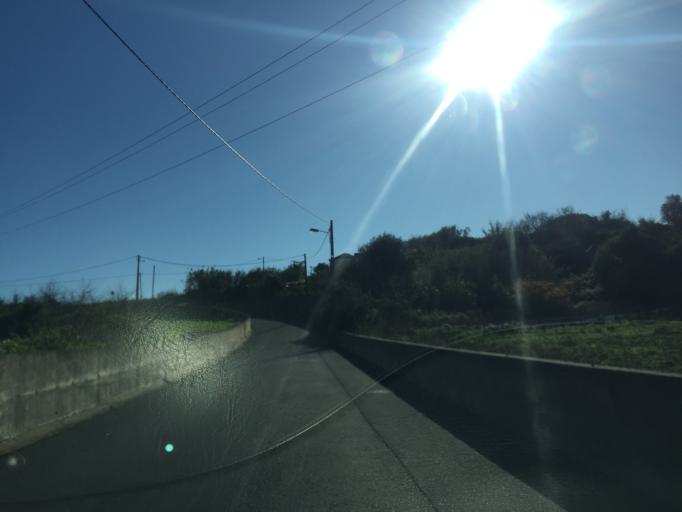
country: PT
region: Lisbon
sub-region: Sintra
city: Pero Pinheiro
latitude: 38.8506
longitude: -9.3181
